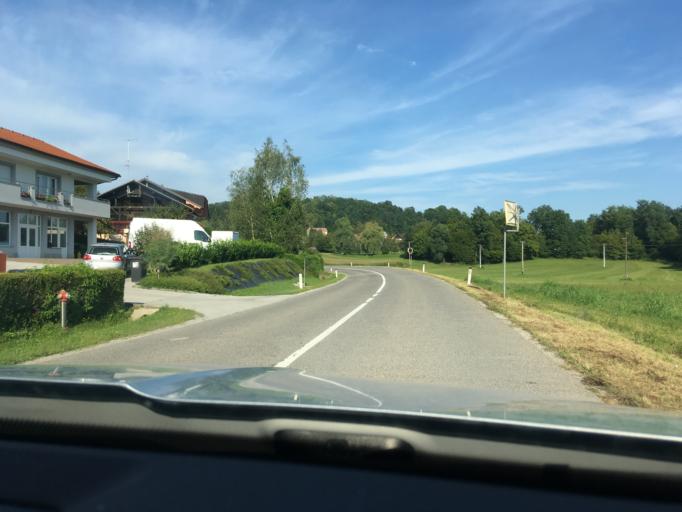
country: SI
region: Metlika
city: Metlika
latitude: 45.6104
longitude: 15.2655
